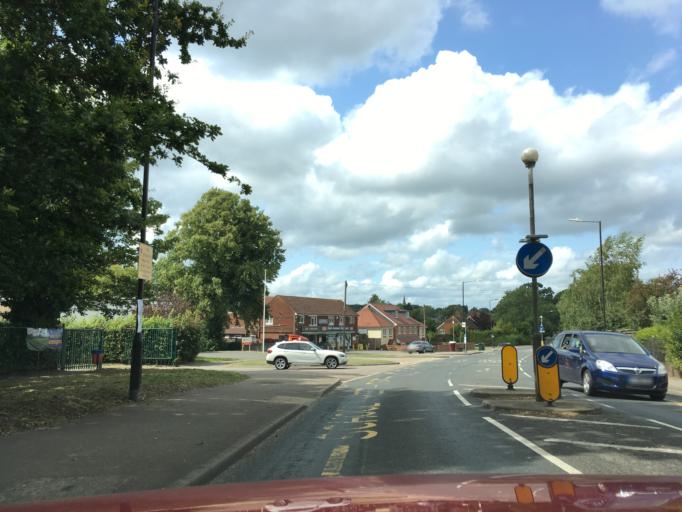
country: GB
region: England
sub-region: Kent
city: Tenterden
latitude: 51.0795
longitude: 0.6952
